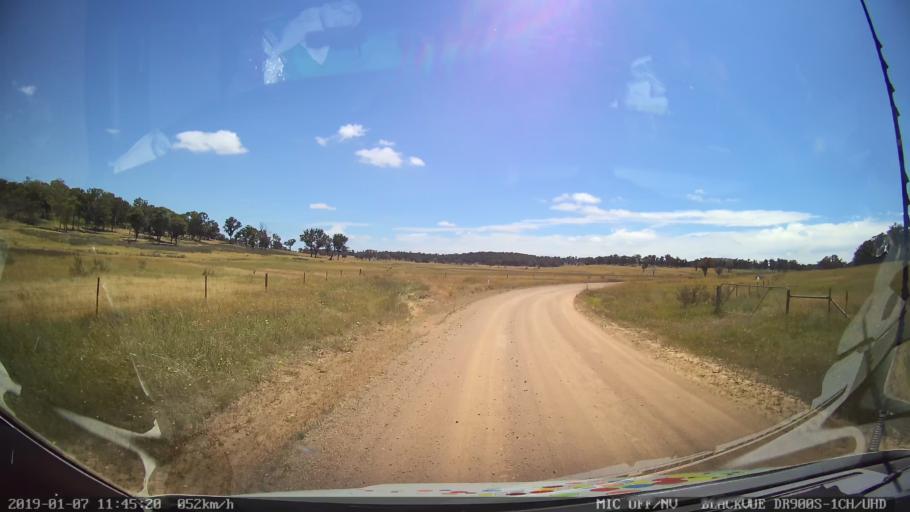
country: AU
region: New South Wales
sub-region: Guyra
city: Guyra
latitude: -30.3466
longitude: 151.6050
